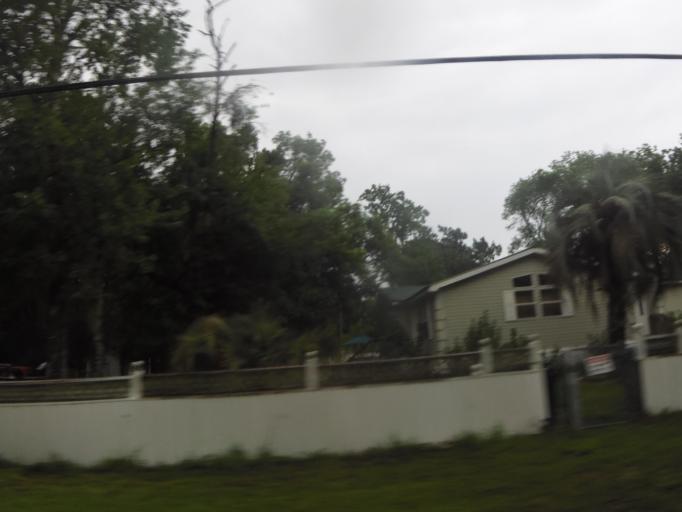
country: US
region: Florida
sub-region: Duval County
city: Jacksonville
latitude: 30.2661
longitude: -81.5776
